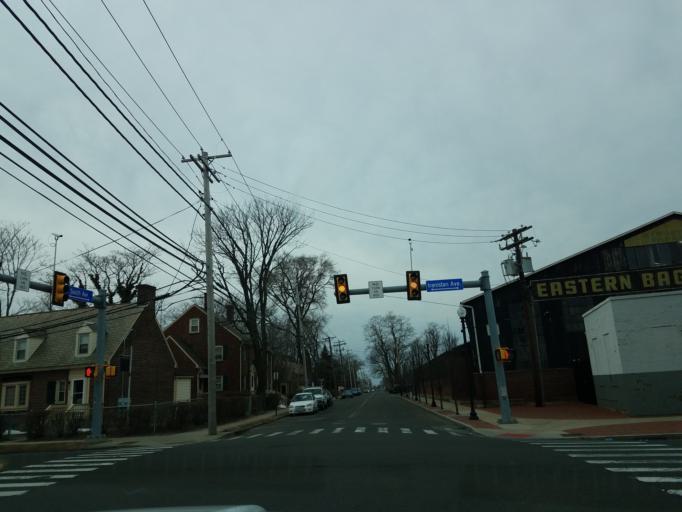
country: US
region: Connecticut
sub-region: Fairfield County
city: Bridgeport
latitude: 41.1672
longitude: -73.1993
